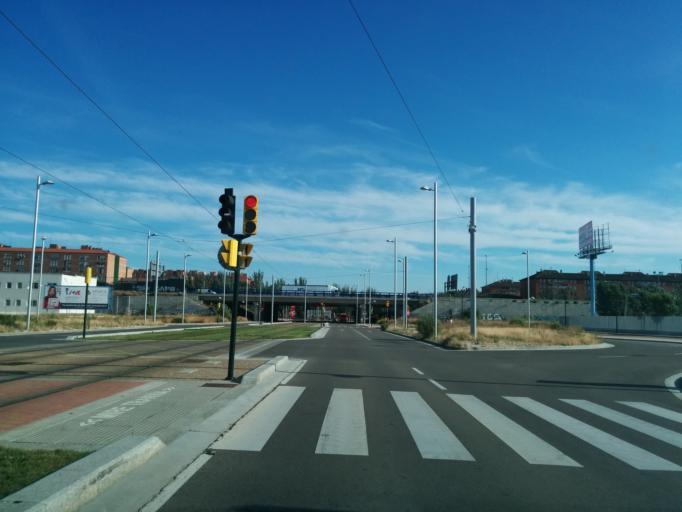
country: ES
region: Aragon
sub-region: Provincia de Zaragoza
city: Almozara
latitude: 41.6816
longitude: -0.8900
